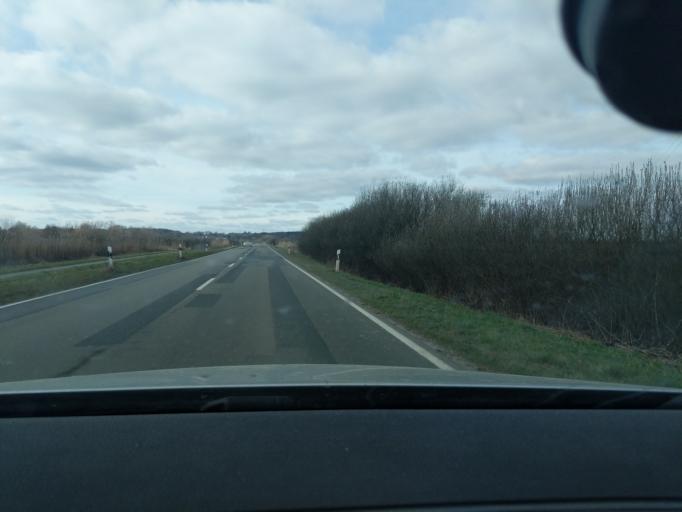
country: DE
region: Lower Saxony
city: Guderhandviertel
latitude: 53.5456
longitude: 9.5854
